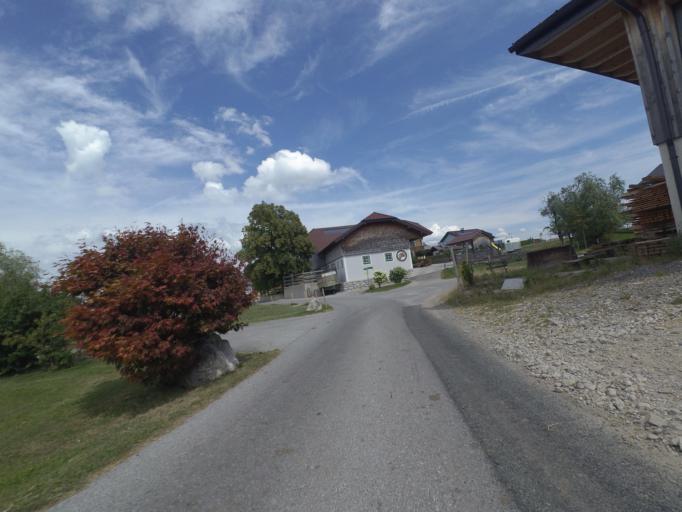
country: AT
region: Salzburg
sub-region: Politischer Bezirk Salzburg-Umgebung
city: Obertrum am See
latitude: 47.9121
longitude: 13.0927
